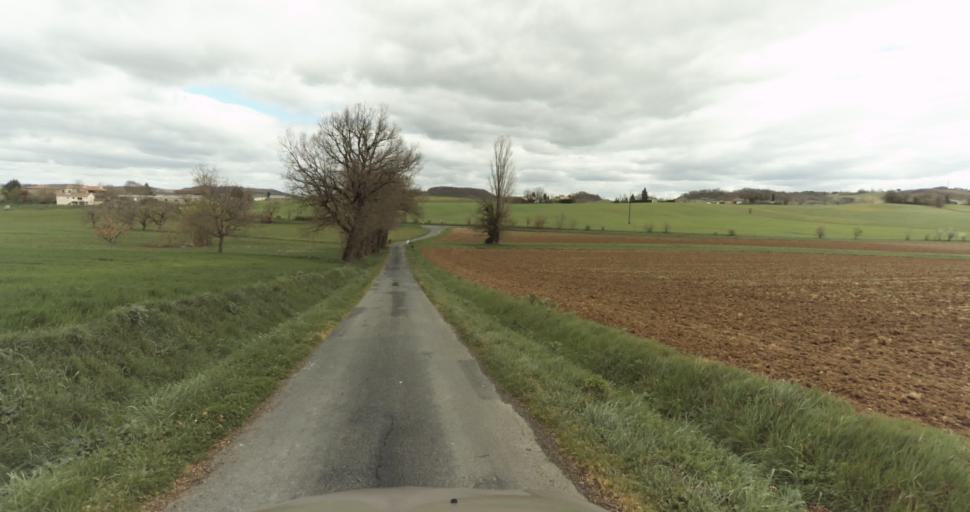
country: FR
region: Midi-Pyrenees
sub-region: Departement du Tarn
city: Puygouzon
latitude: 43.8765
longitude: 2.1703
